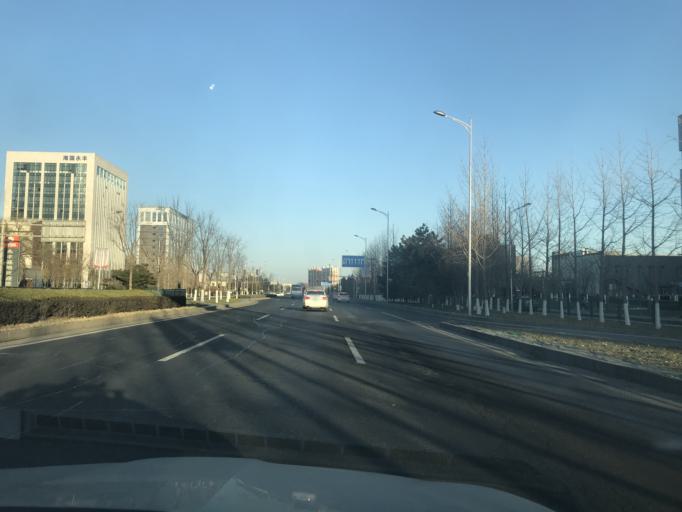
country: CN
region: Beijing
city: Xibeiwang
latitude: 40.0735
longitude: 116.2424
